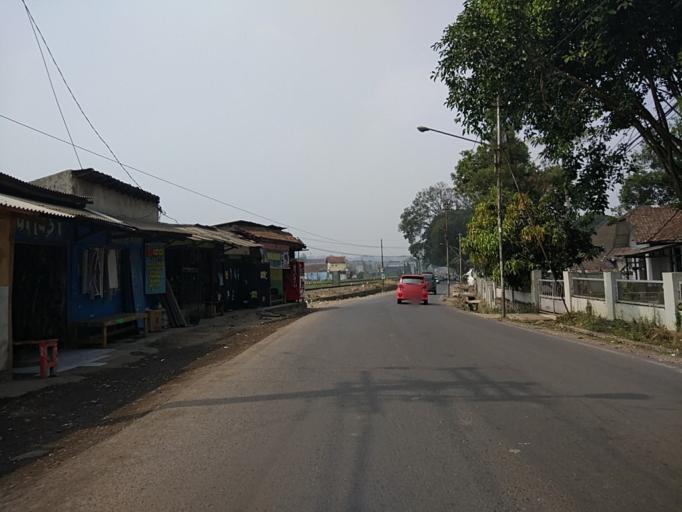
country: ID
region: West Java
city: Padalarang
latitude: -6.8379
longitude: 107.4918
